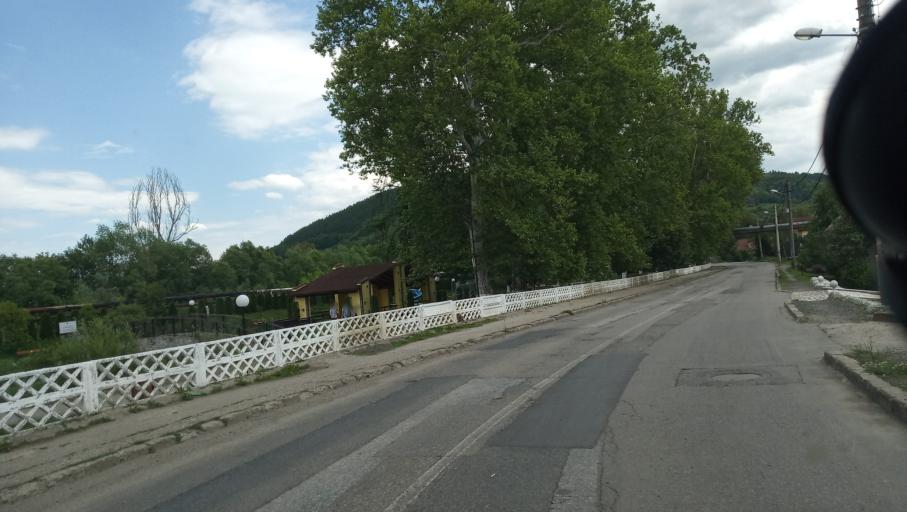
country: RO
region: Hunedoara
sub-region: Municipiul Brad
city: Brad
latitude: 46.1266
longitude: 22.7952
